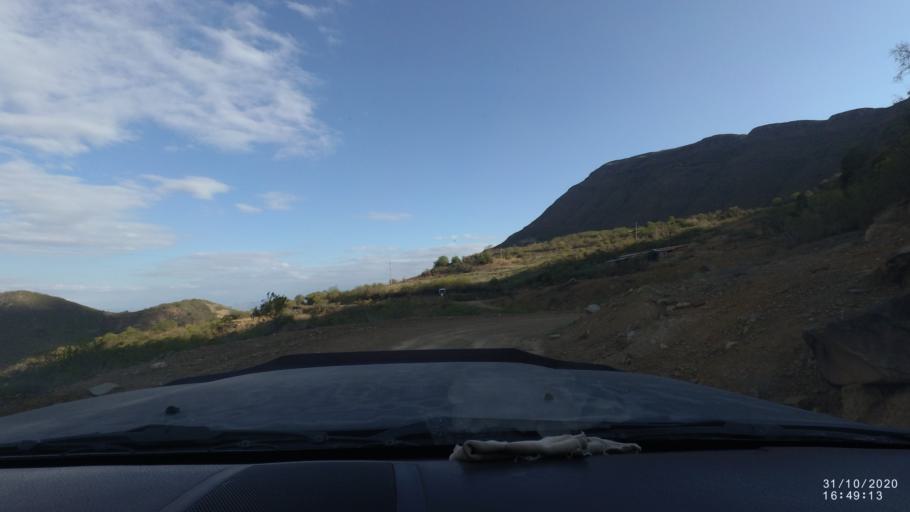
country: BO
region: Chuquisaca
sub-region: Provincia Zudanez
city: Mojocoya
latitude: -18.5062
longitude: -64.5720
